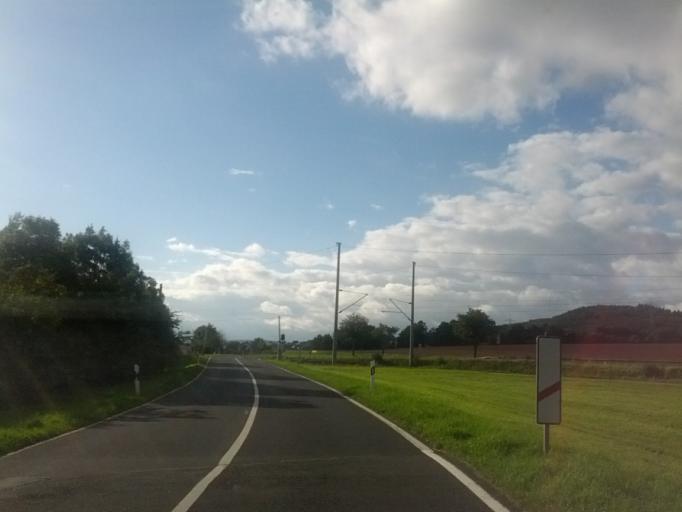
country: DE
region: Hesse
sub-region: Regierungsbezirk Kassel
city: Herleshausen
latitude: 51.0019
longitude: 10.1874
